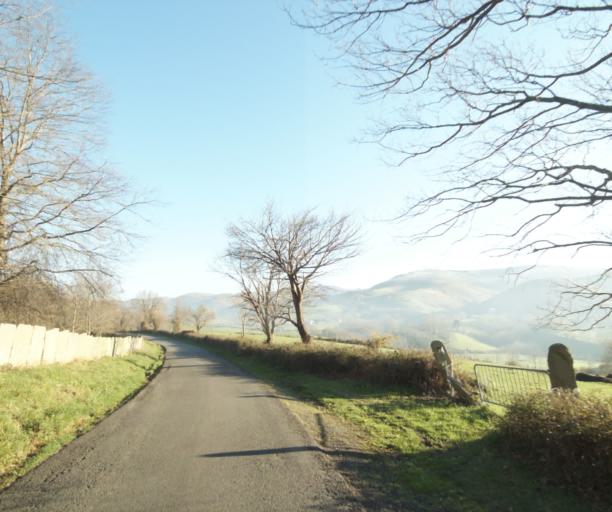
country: FR
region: Aquitaine
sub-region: Departement des Pyrenees-Atlantiques
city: Urrugne
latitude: 43.3489
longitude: -1.7072
